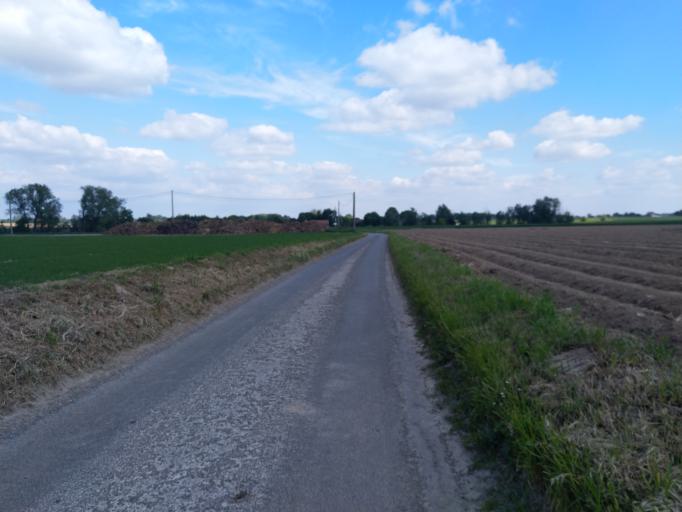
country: BE
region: Wallonia
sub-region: Province du Hainaut
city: Soignies
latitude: 50.5868
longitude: 4.0265
